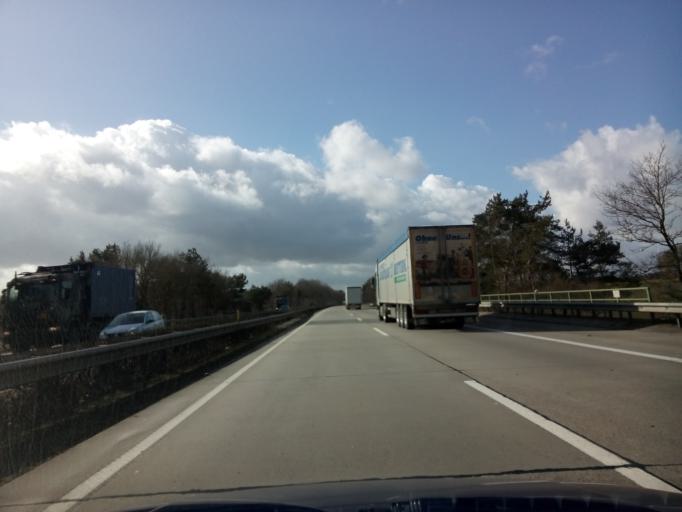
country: DE
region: Lower Saxony
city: Visbek
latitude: 52.8956
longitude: 8.3274
